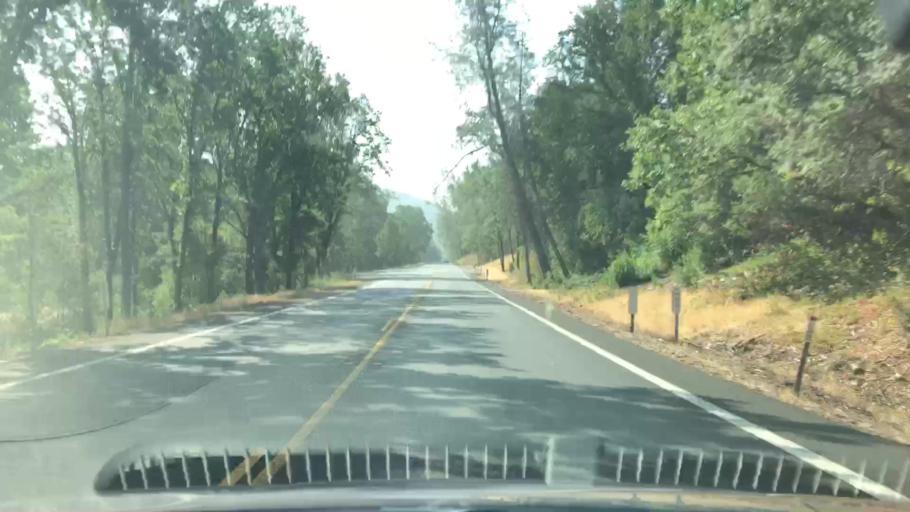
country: US
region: California
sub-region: Lake County
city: Middletown
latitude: 38.7046
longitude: -122.6057
